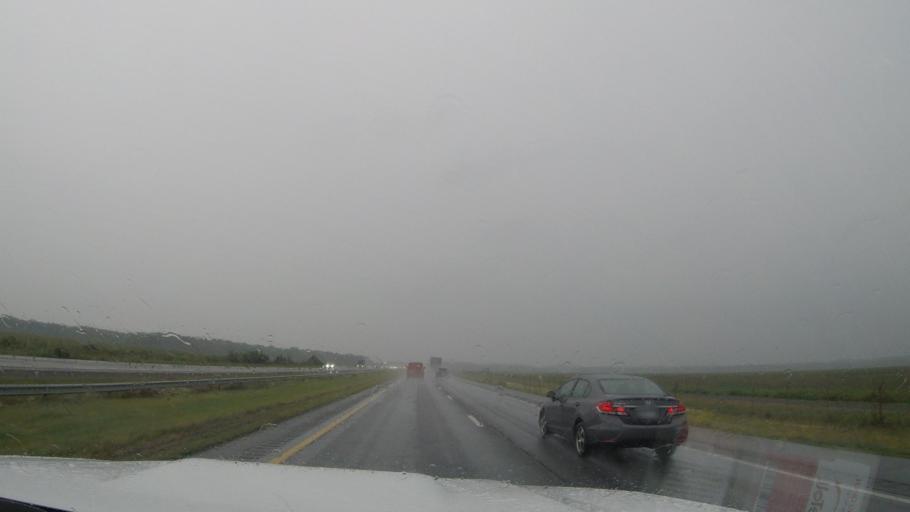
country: US
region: New York
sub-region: Seneca County
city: Bridgeport
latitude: 42.9879
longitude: -76.7640
